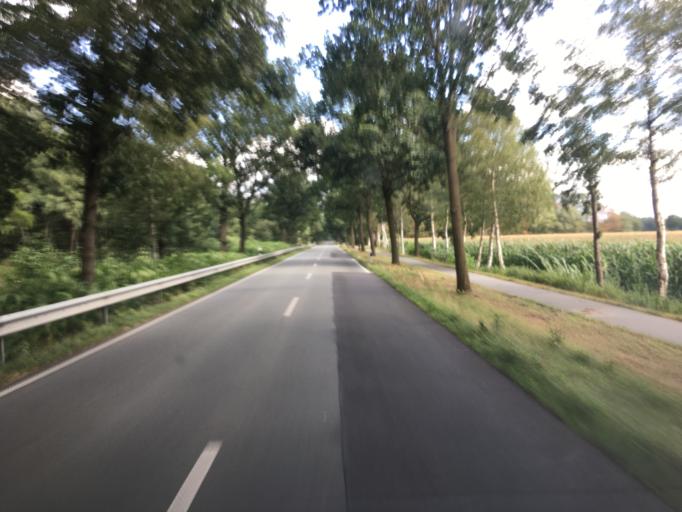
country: DE
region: Lower Saxony
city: Friesoythe
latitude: 53.0848
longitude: 7.8135
